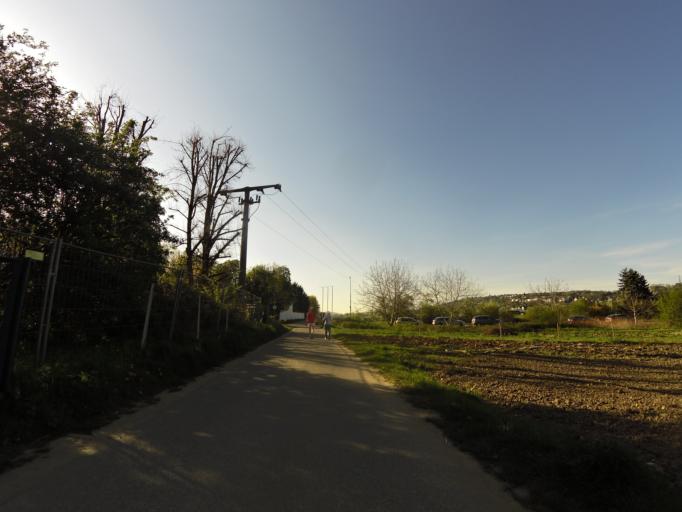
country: DE
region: Rheinland-Pfalz
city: Niederwerth
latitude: 50.3922
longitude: 7.6071
